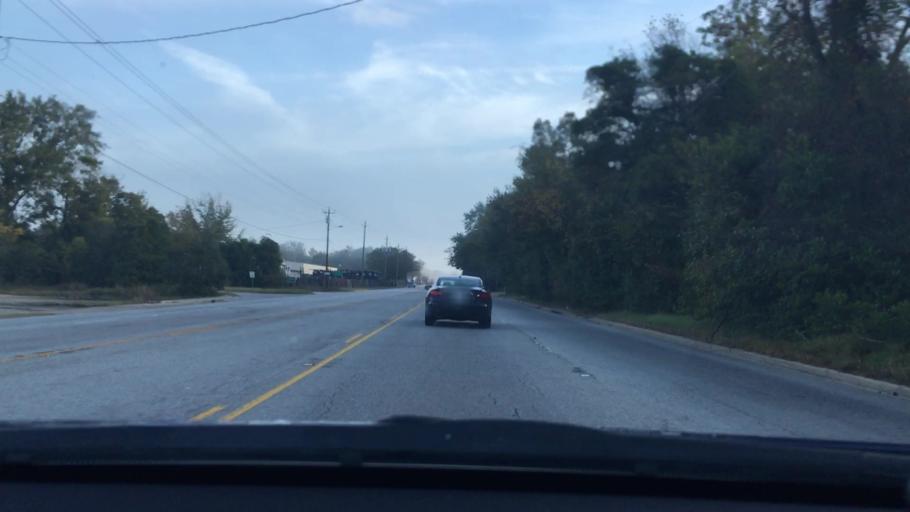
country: US
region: South Carolina
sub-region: Sumter County
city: South Sumter
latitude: 33.8899
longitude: -80.3440
